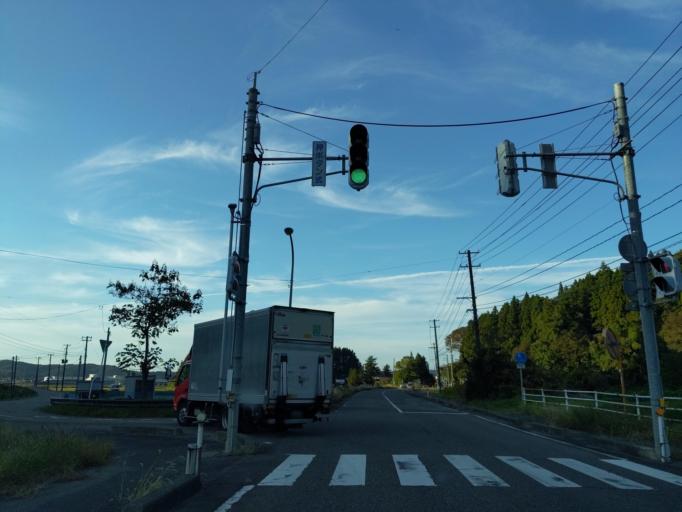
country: JP
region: Niigata
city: Nagaoka
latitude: 37.5740
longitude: 138.7858
